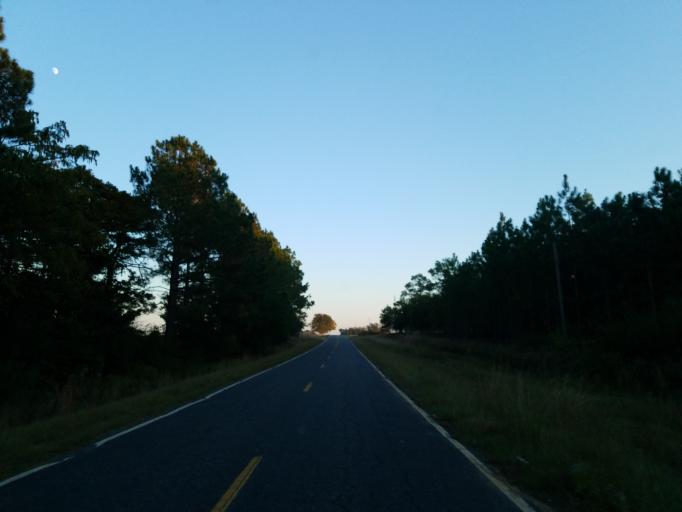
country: US
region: Georgia
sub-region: Ben Hill County
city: Fitzgerald
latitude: 31.6742
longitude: -83.4017
